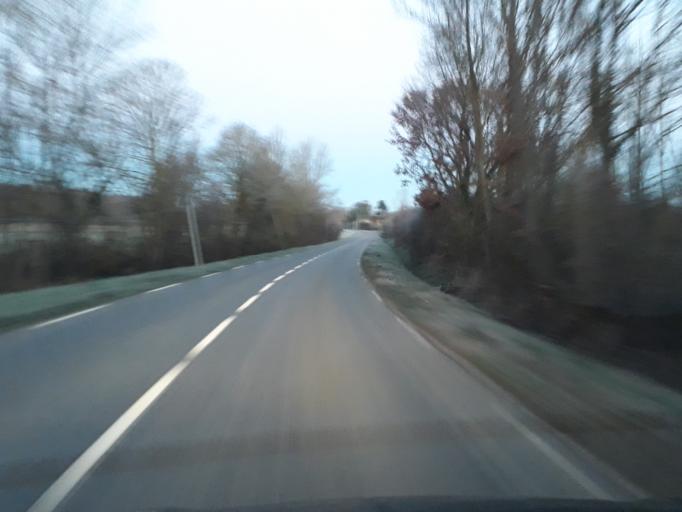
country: FR
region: Midi-Pyrenees
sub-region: Departement du Gers
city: Samatan
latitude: 43.4743
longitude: 0.9554
